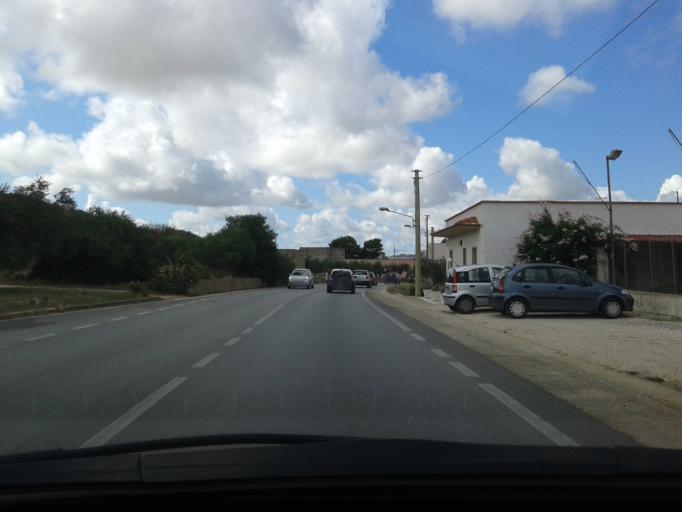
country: IT
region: Sicily
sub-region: Trapani
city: Custonaci
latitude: 38.0775
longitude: 12.6982
